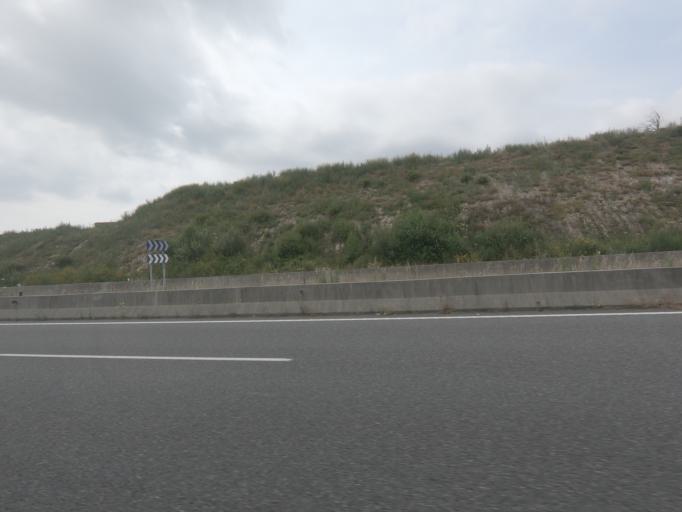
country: ES
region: Galicia
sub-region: Provincia de Pontevedra
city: Covelo
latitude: 42.1659
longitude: -8.3850
